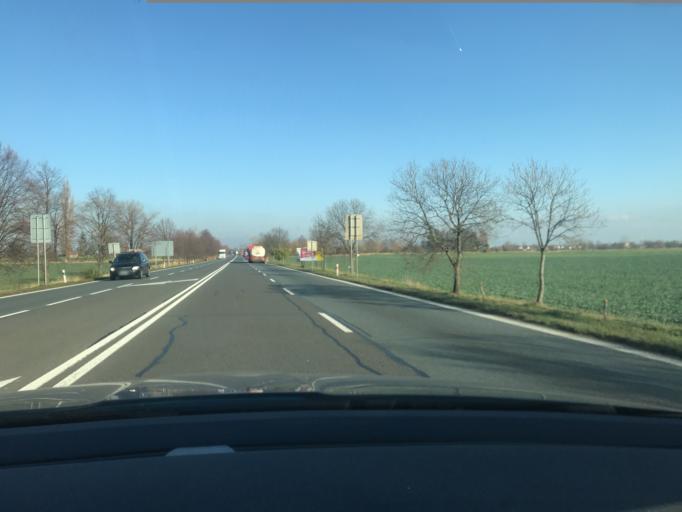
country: CZ
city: Stezery
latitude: 50.2117
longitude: 15.7834
